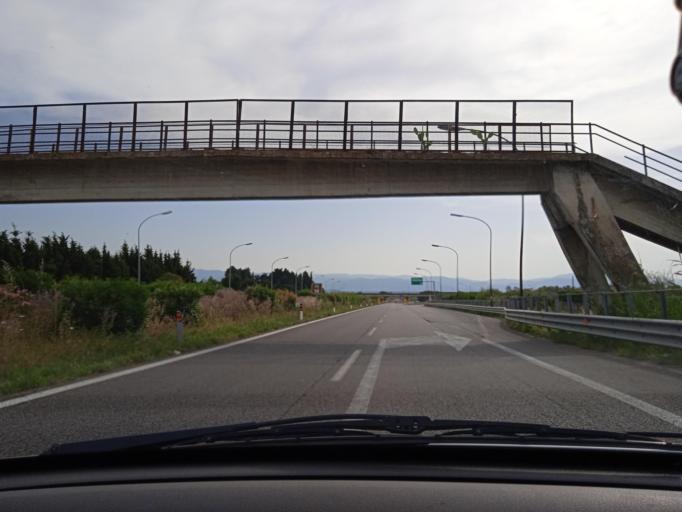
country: IT
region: Sicily
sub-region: Messina
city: Barcellona Pozzo di Gotto
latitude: 38.1588
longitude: 15.1925
